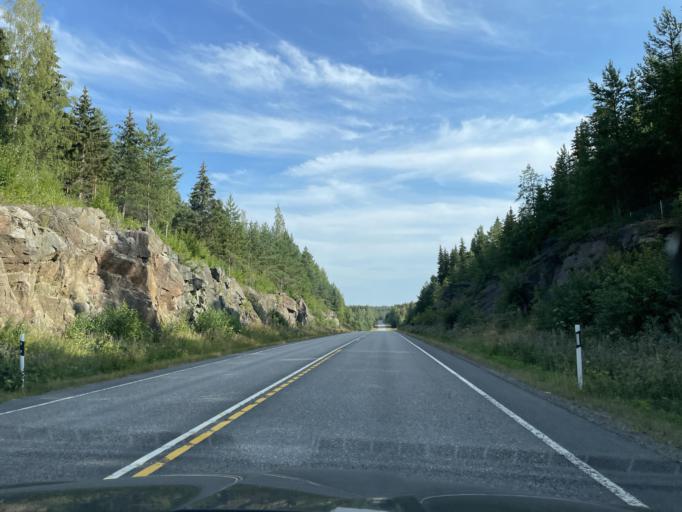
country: FI
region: Central Finland
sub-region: Jaemsae
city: Jaemsae
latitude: 61.7876
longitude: 25.2189
